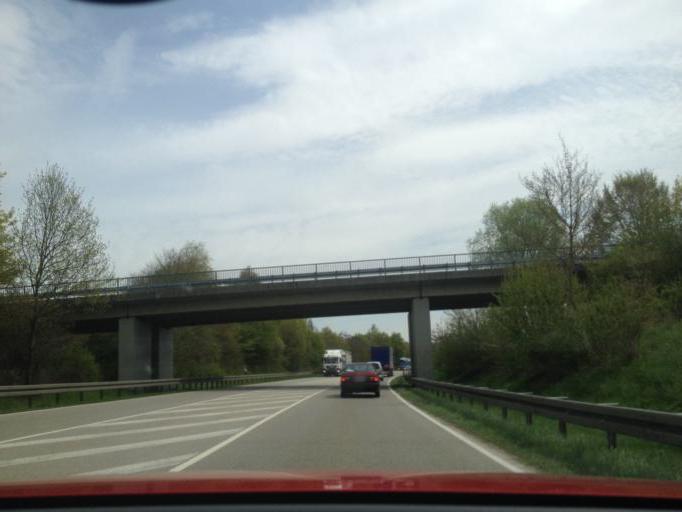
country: DE
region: Bavaria
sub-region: Upper Bavaria
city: Reichertshofen
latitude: 48.6488
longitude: 11.4991
